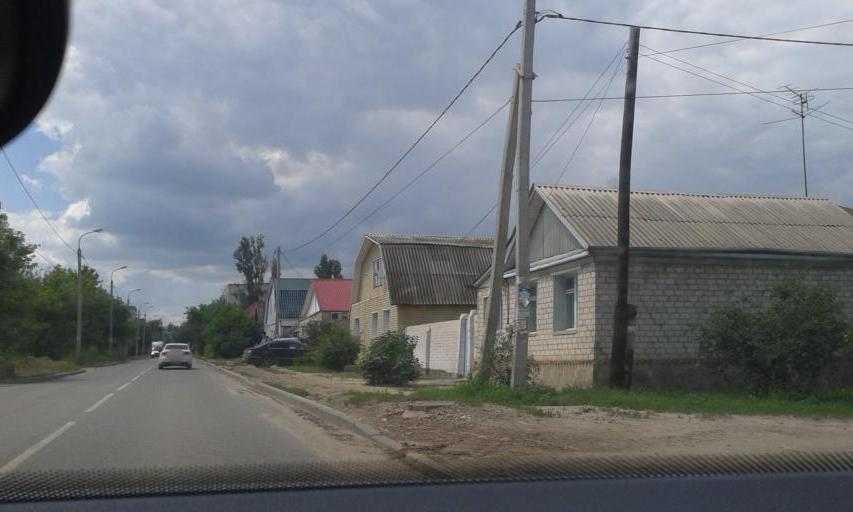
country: RU
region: Volgograd
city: Gorodishche
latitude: 48.7724
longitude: 44.4871
